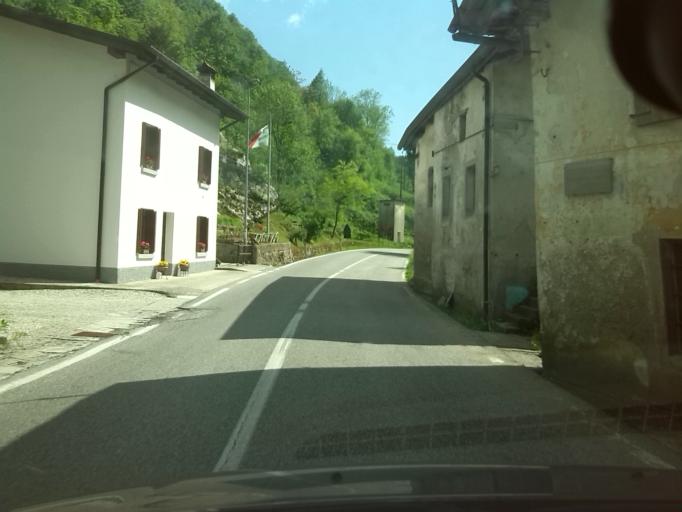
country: IT
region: Friuli Venezia Giulia
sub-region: Provincia di Udine
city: Pulfero
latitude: 46.1999
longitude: 13.4712
